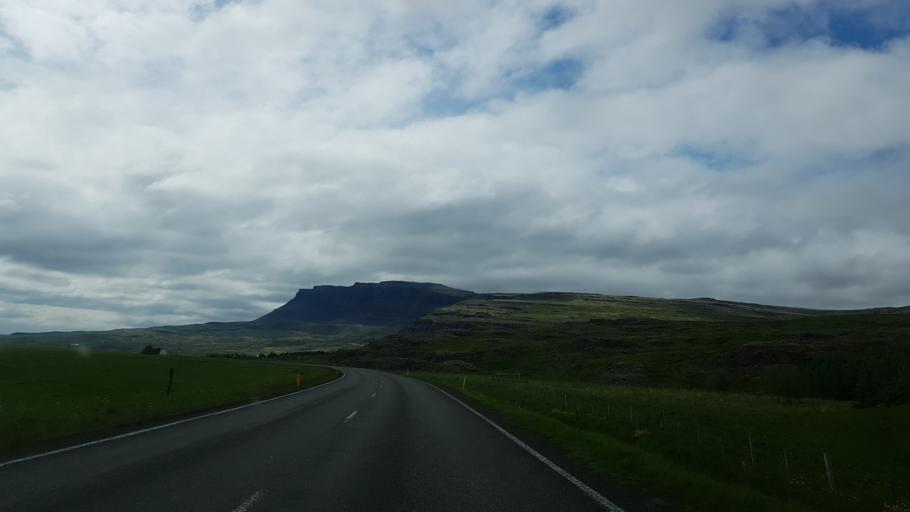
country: IS
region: West
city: Borgarnes
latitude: 64.8041
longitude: -21.4509
